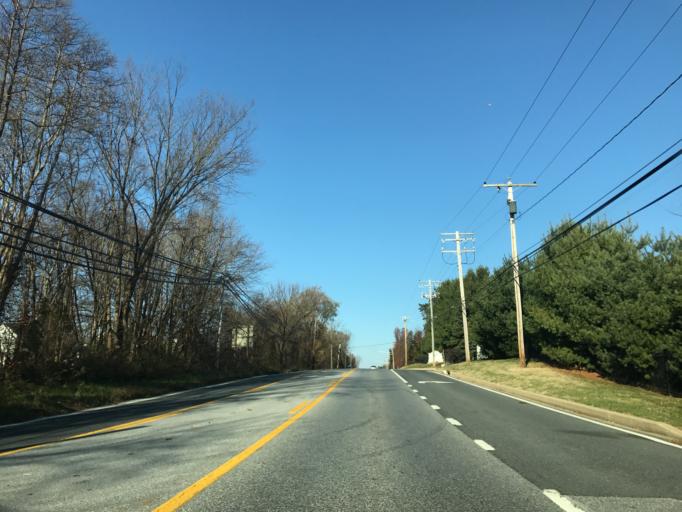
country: US
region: Maryland
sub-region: Howard County
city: Ellicott City
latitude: 39.2478
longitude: -76.8090
